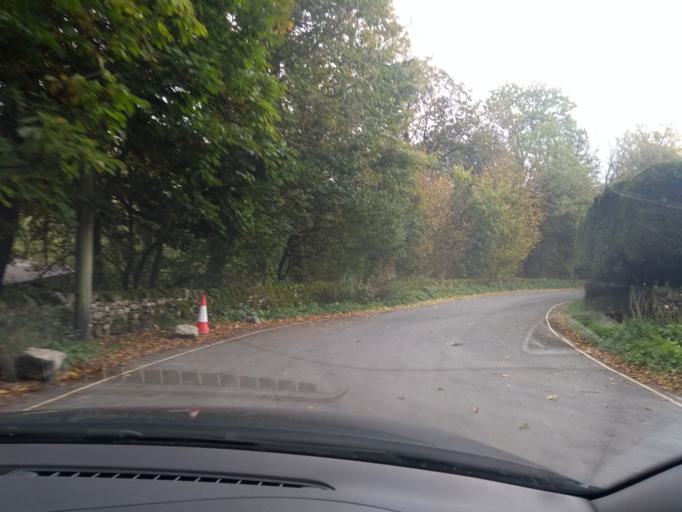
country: GB
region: England
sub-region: North Yorkshire
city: Gargrave
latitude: 54.0645
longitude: -2.1554
